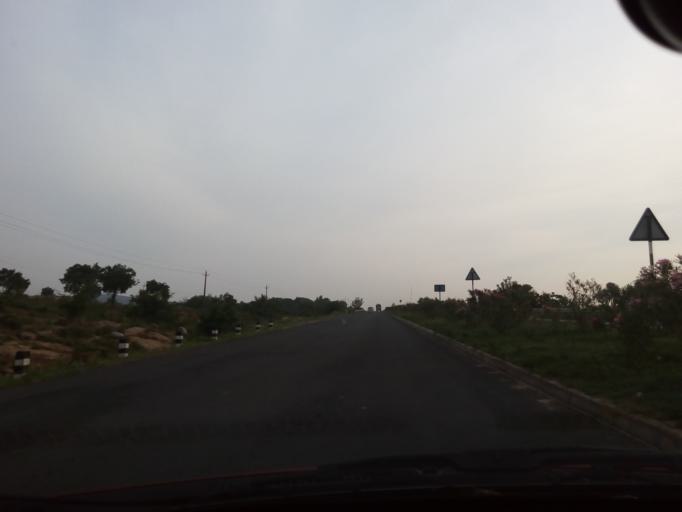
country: IN
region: Karnataka
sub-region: Chikkaballapur
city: Gudibanda
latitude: 13.6029
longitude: 77.7869
